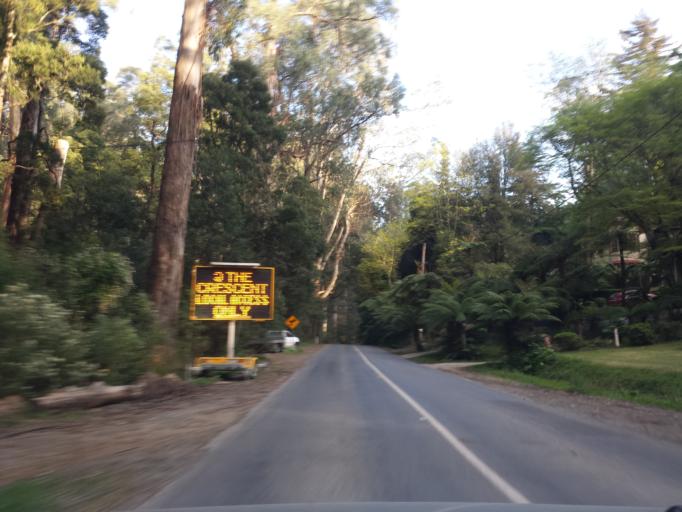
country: AU
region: Victoria
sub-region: Yarra Ranges
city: Kallista
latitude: -37.8777
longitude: 145.3727
